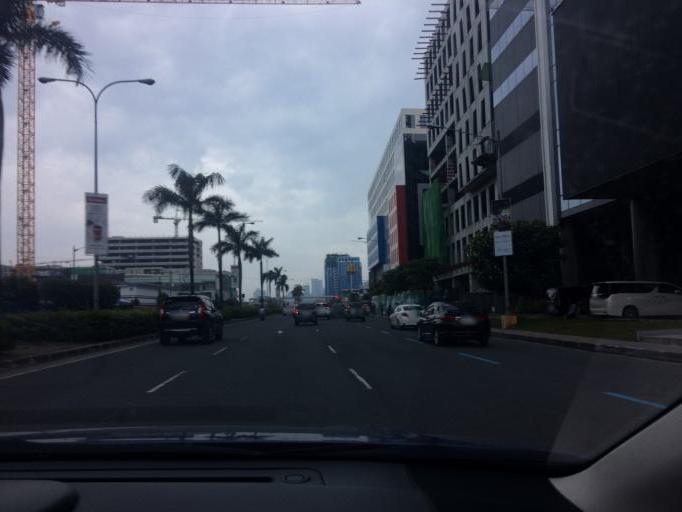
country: PH
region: Metro Manila
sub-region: Makati City
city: Makati City
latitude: 14.5342
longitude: 120.9893
